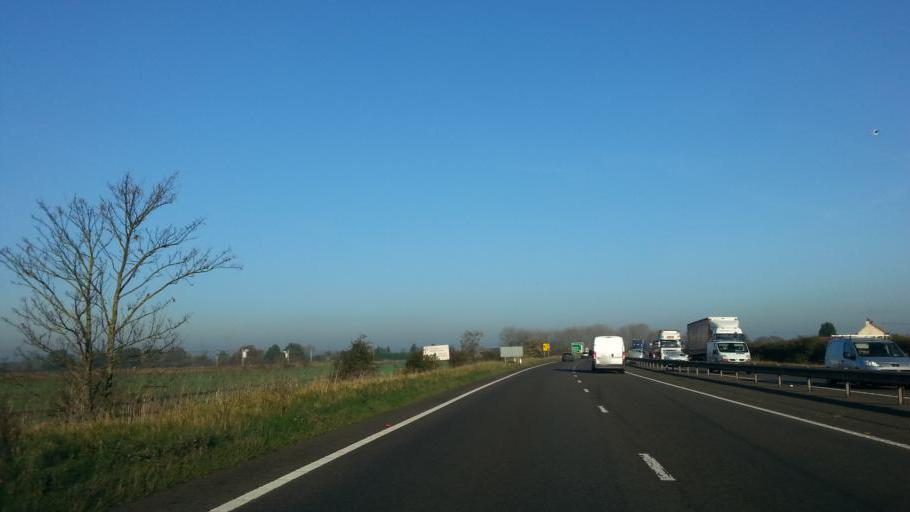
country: GB
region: England
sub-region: Nottinghamshire
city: Newark on Trent
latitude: 53.1126
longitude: -0.8150
